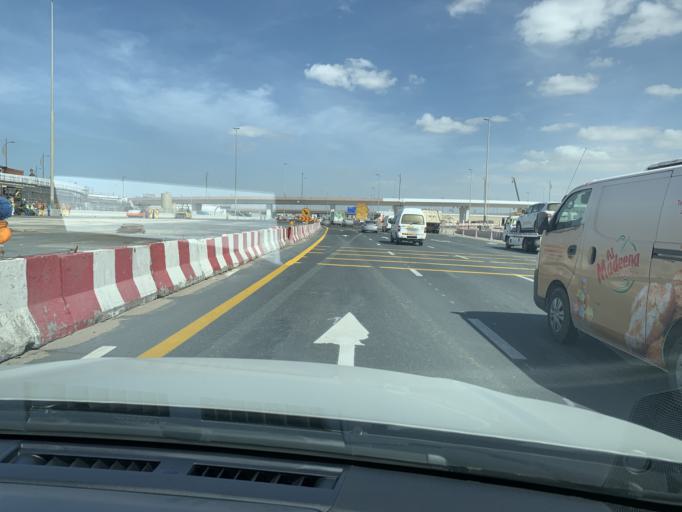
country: AE
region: Dubai
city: Dubai
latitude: 24.9706
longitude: 55.1416
